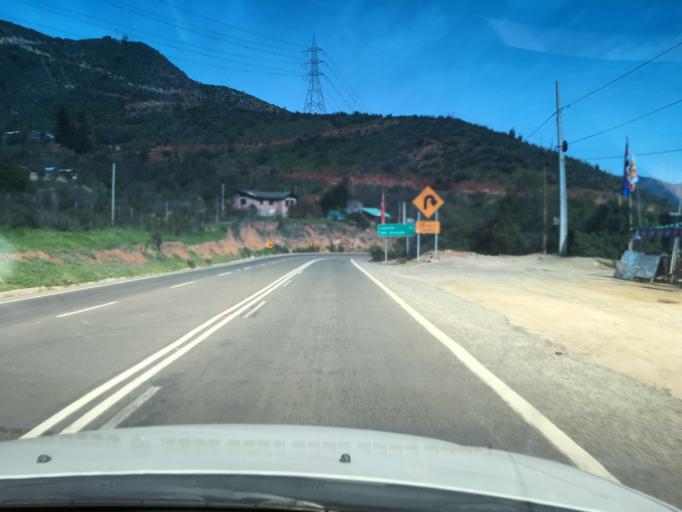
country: CL
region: Valparaiso
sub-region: Provincia de Marga Marga
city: Limache
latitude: -33.0602
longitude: -71.0533
